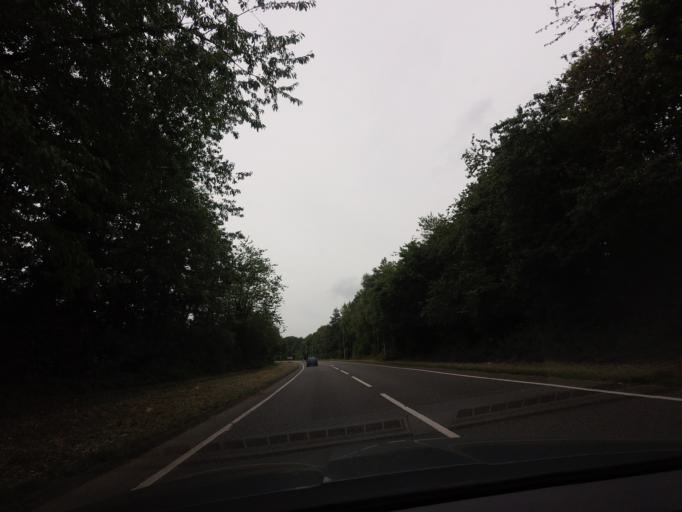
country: GB
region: England
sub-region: Telford and Wrekin
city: Ironbridge
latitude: 52.6446
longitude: -2.4700
